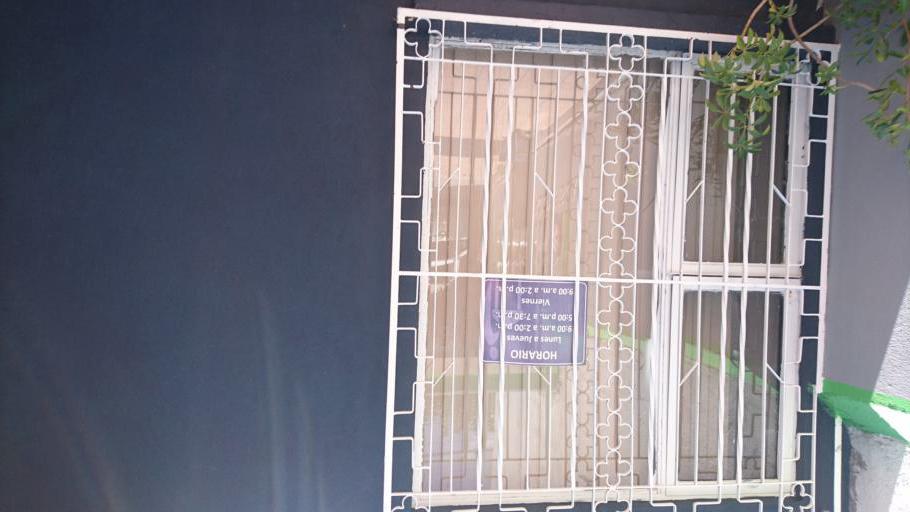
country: MX
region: San Luis Potosi
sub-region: San Luis Potosi
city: San Luis Potosi
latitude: 22.1434
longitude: -100.9869
